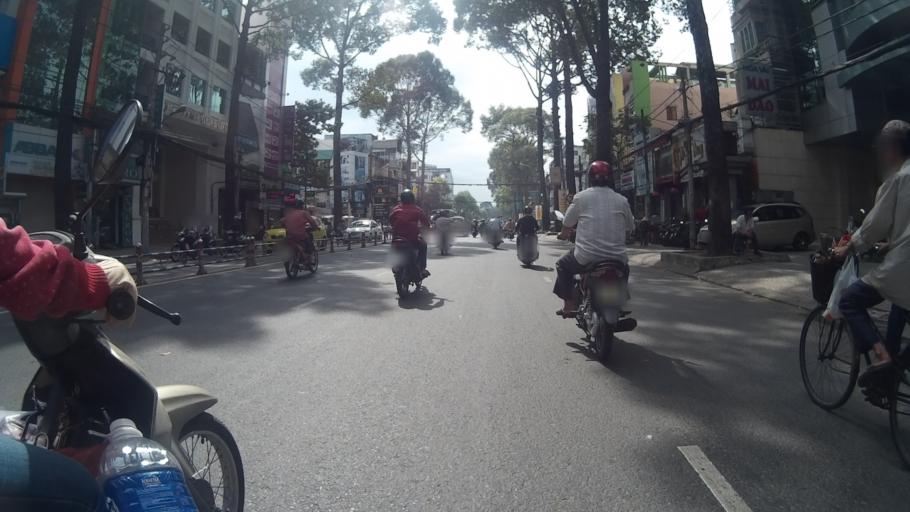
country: VN
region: Ho Chi Minh City
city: Quan Ba
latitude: 10.7743
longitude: 106.6783
